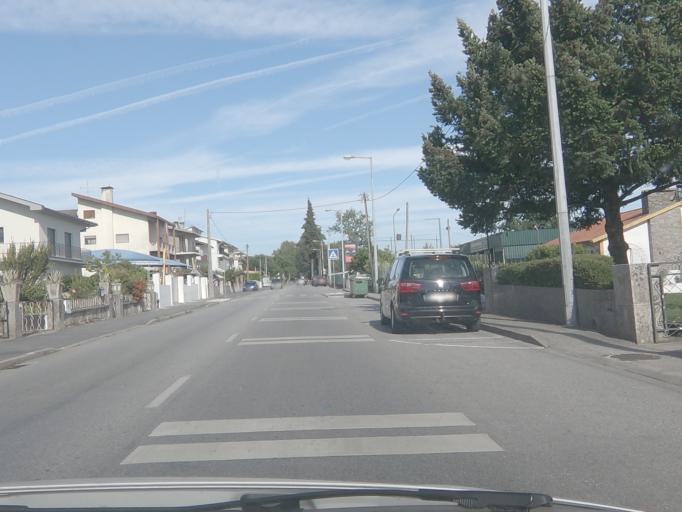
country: PT
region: Viseu
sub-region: Viseu
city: Viseu
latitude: 40.6544
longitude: -7.8949
